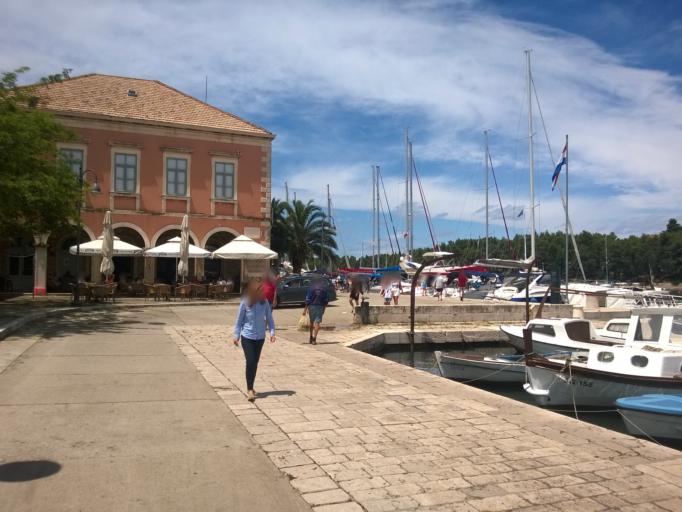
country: HR
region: Splitsko-Dalmatinska
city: Stari Grad
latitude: 43.1838
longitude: 16.5955
